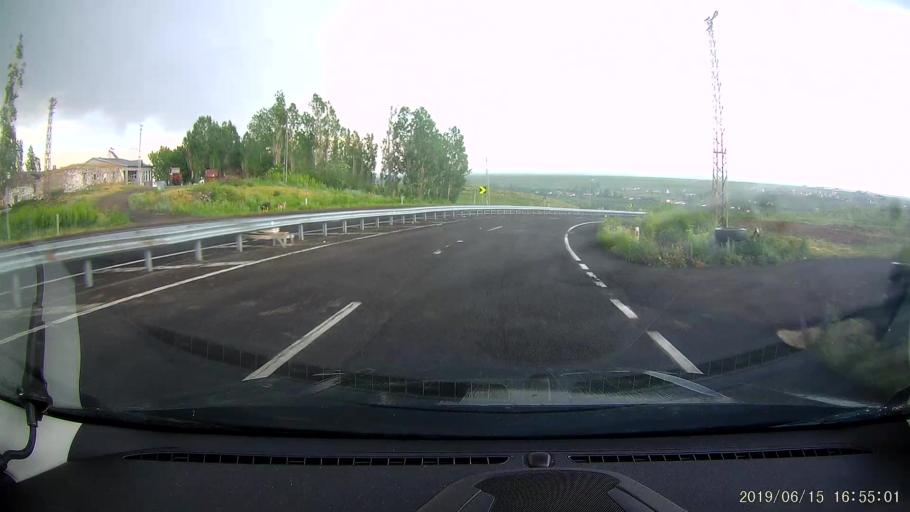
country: TR
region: Kars
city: Susuz
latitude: 40.7869
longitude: 43.1359
